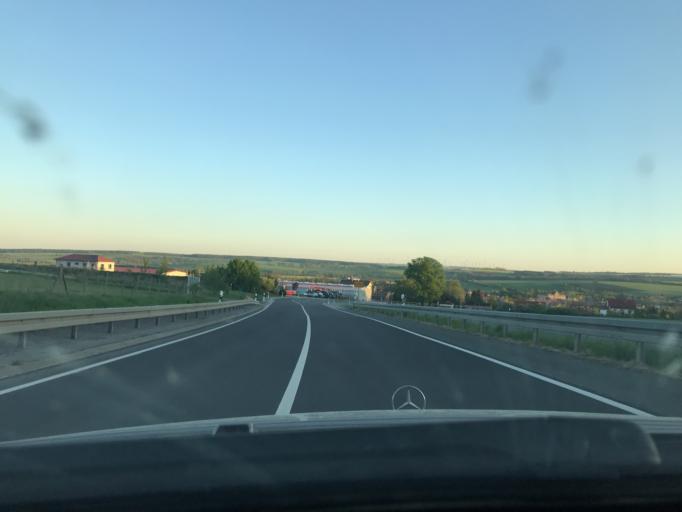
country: DE
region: Thuringia
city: Dingelstadt
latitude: 51.3268
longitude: 10.3224
